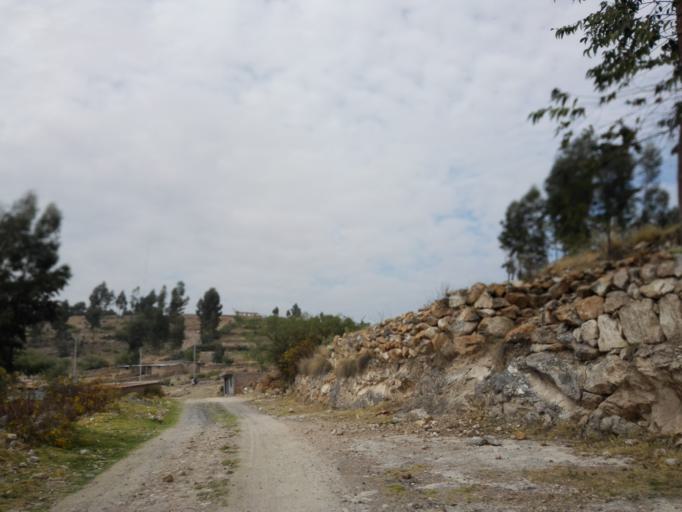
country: PE
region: Ayacucho
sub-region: Provincia de Huamanga
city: Ayacucho
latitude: -13.1480
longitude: -74.2373
